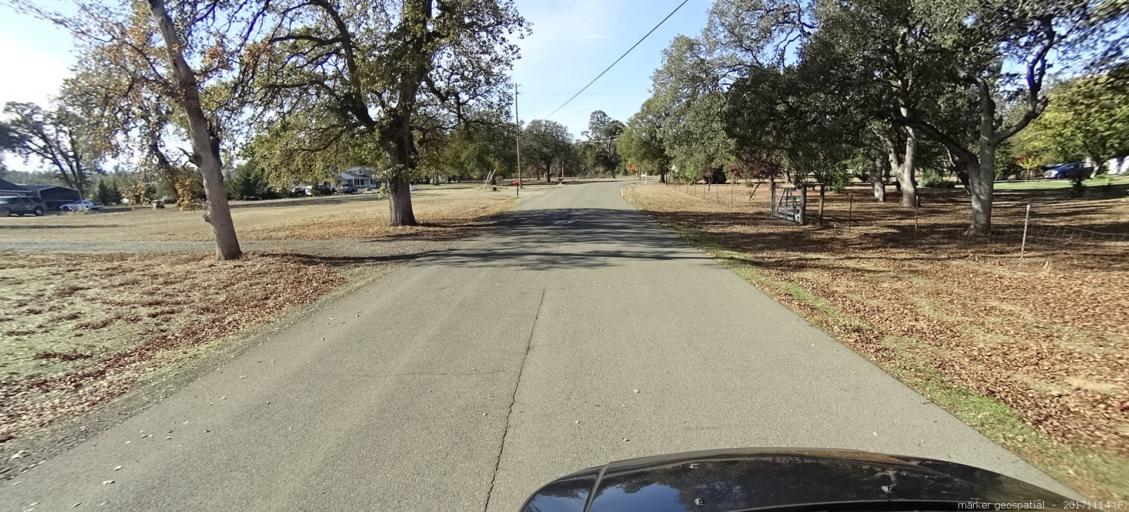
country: US
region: California
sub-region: Shasta County
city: Anderson
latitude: 40.3805
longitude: -122.4503
